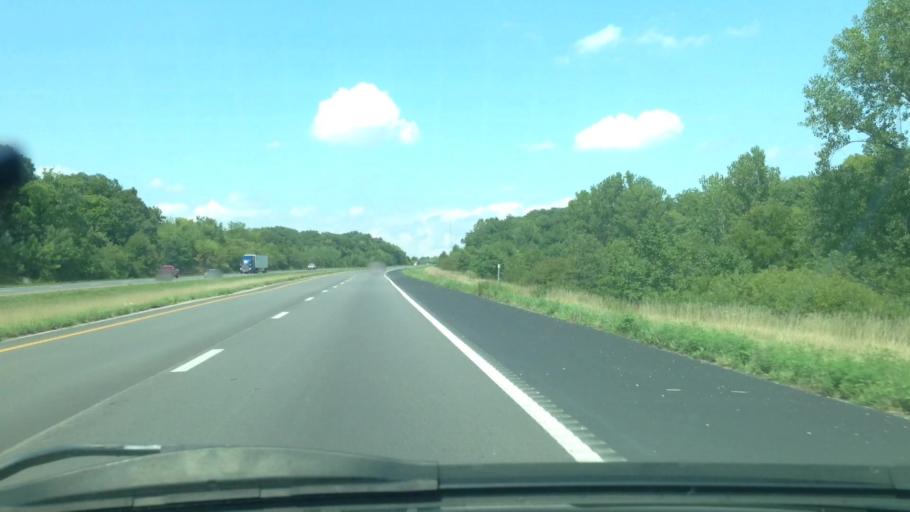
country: US
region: Missouri
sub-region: Lincoln County
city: Troy
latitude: 39.0342
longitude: -90.9775
